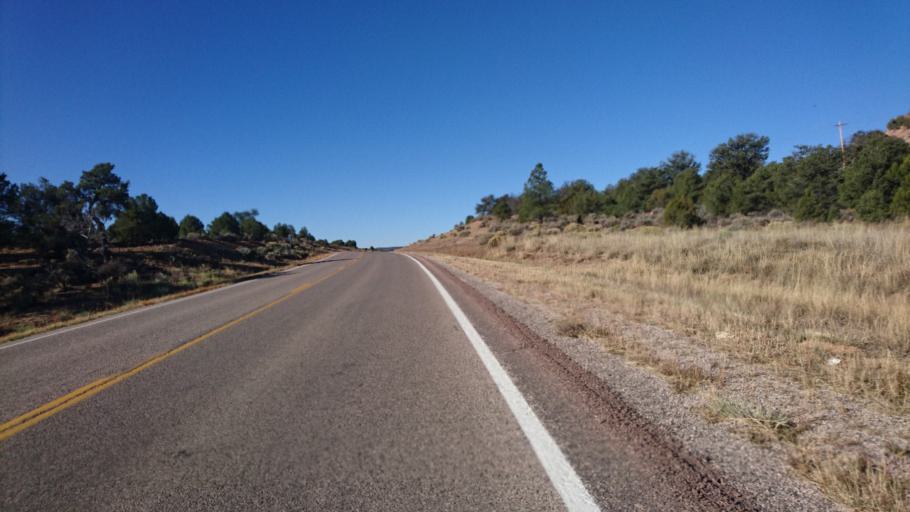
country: US
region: New Mexico
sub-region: McKinley County
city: Black Rock
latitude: 35.1247
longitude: -108.5356
